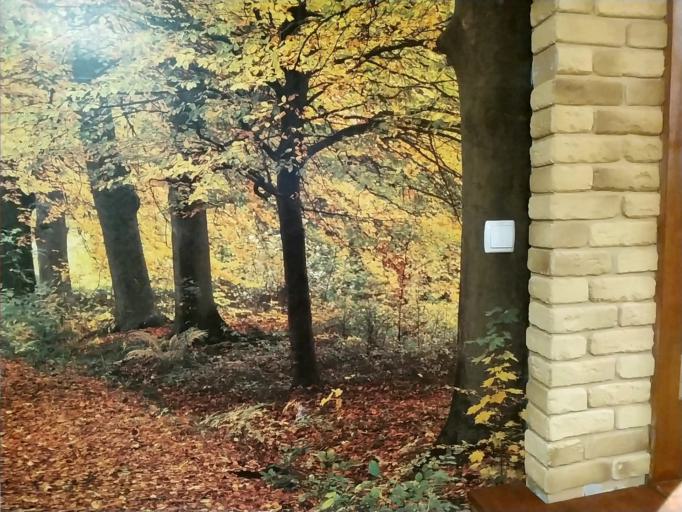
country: RU
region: Smolensk
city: Safonovo
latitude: 55.1978
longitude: 33.1786
